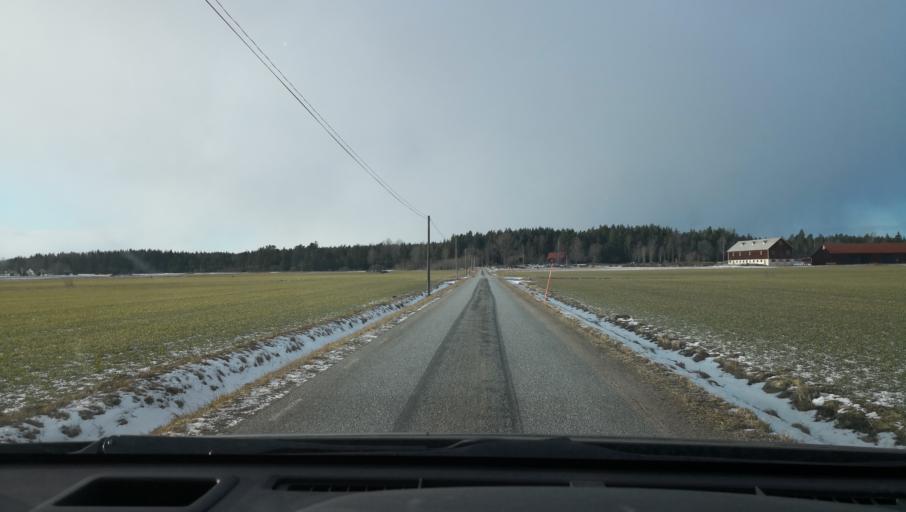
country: SE
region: Uppsala
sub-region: Enkopings Kommun
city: Irsta
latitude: 59.7063
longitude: 16.9166
